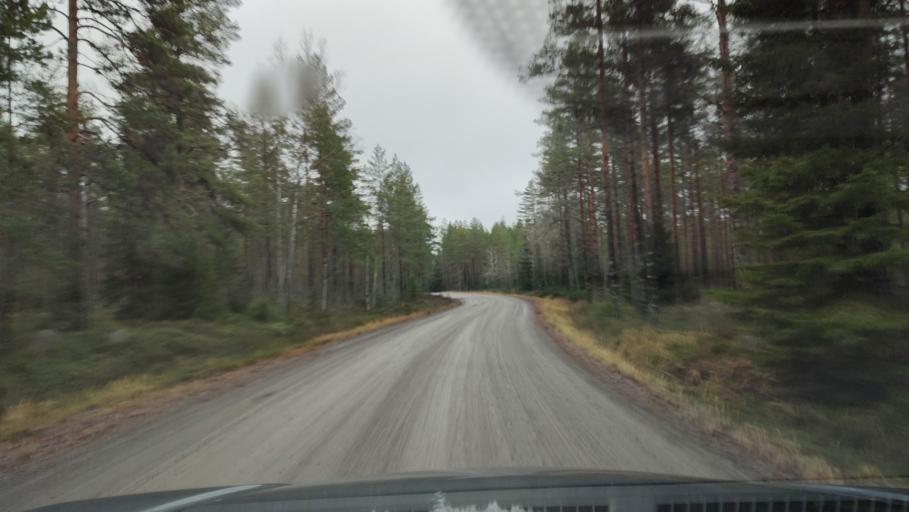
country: FI
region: Southern Ostrobothnia
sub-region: Suupohja
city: Karijoki
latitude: 62.1323
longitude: 21.6228
